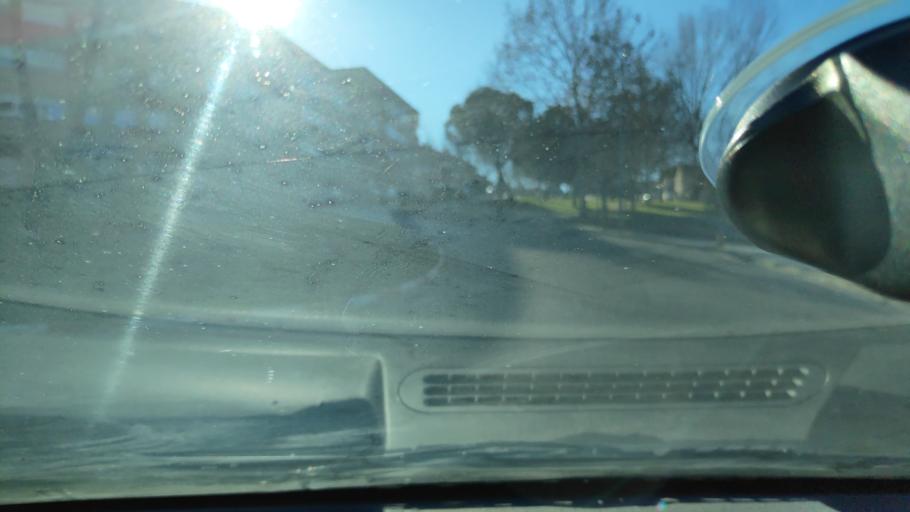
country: ES
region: Catalonia
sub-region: Provincia de Barcelona
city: Sant Quirze del Valles
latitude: 41.5306
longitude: 2.0747
